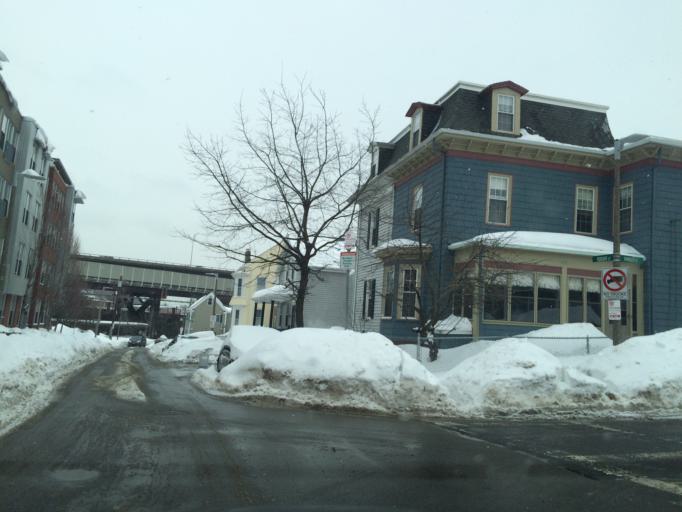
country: US
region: Massachusetts
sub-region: Middlesex County
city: Somerville
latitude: 42.3842
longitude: -71.0785
